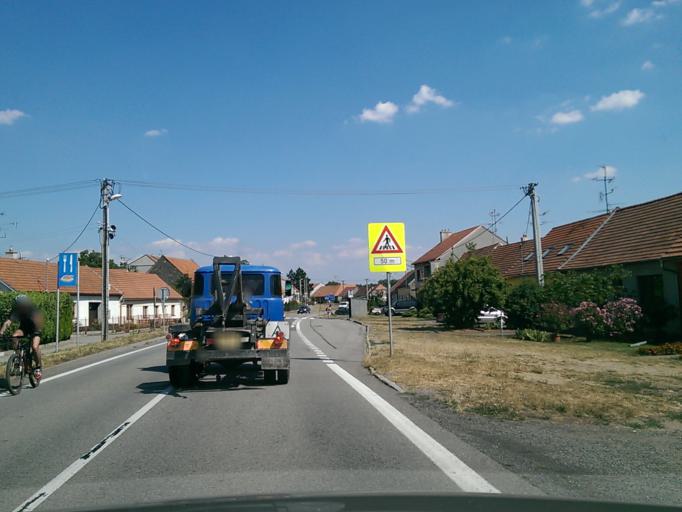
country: AT
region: Lower Austria
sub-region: Politischer Bezirk Mistelbach
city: Drasenhofen
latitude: 48.7794
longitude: 16.6903
